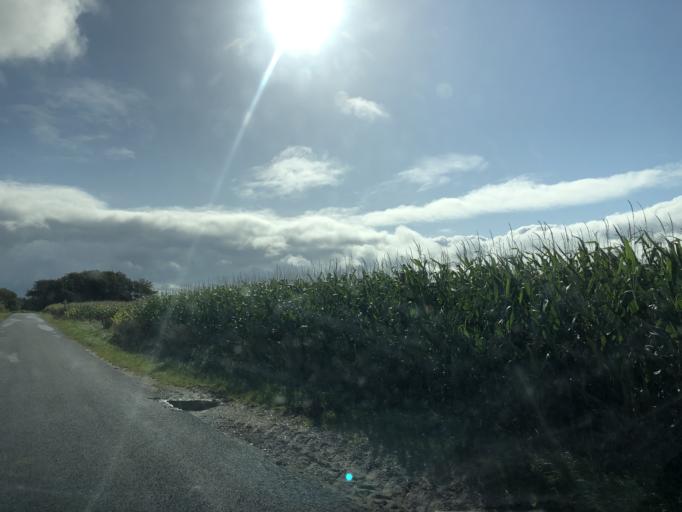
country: DK
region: Central Jutland
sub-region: Holstebro Kommune
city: Ulfborg
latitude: 56.3014
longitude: 8.4576
